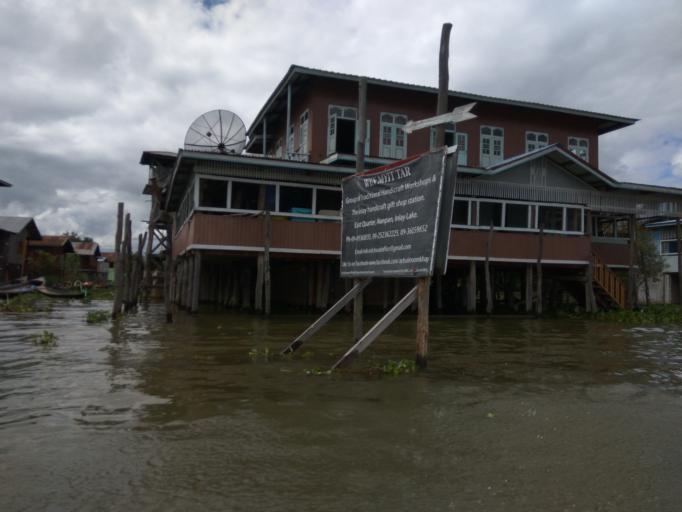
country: MM
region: Shan
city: Taunggyi
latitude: 20.4565
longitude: 96.9072
